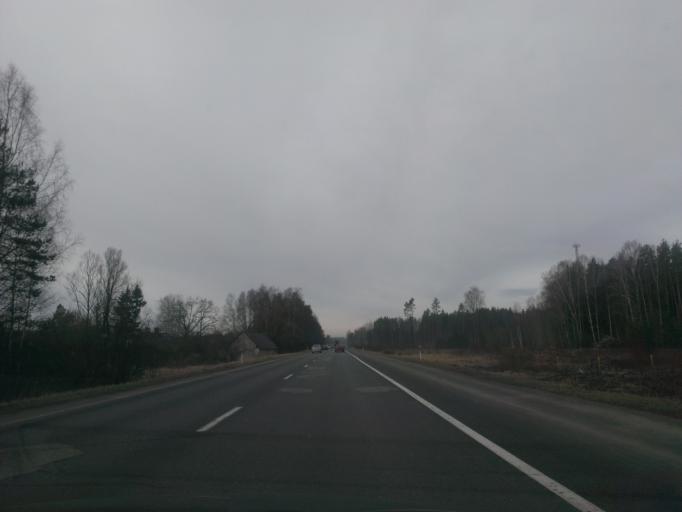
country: LV
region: Incukalns
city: Vangazi
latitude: 57.0958
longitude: 24.5700
